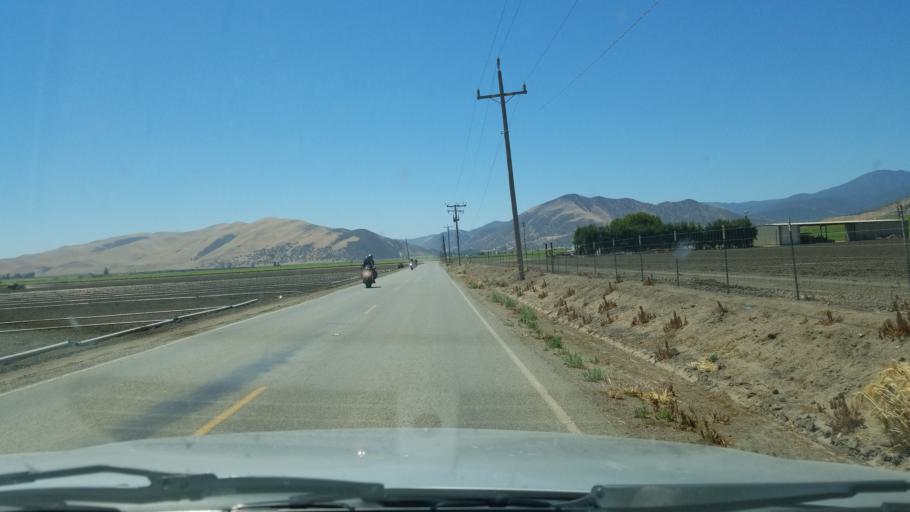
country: US
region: California
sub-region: Monterey County
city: Greenfield
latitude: 36.3215
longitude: -121.3130
